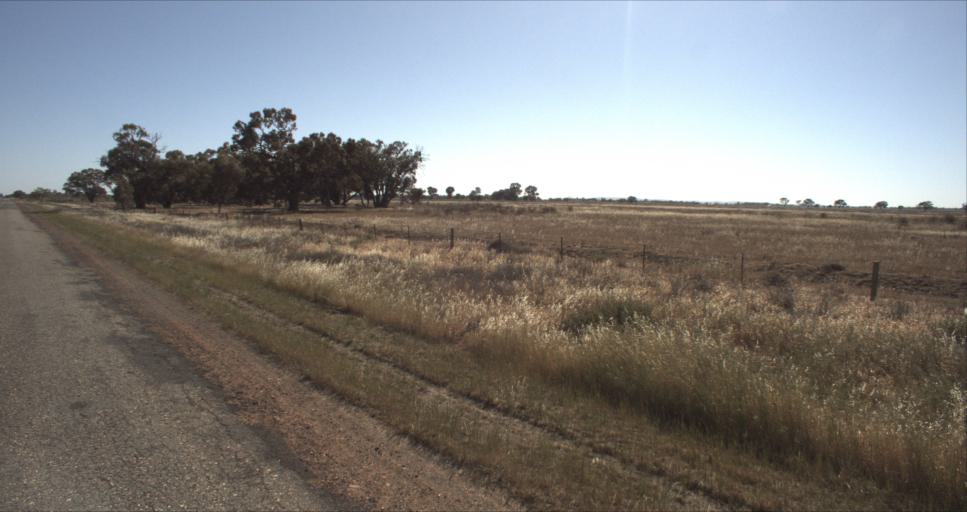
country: AU
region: New South Wales
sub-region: Leeton
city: Leeton
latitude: -34.5910
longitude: 146.2597
